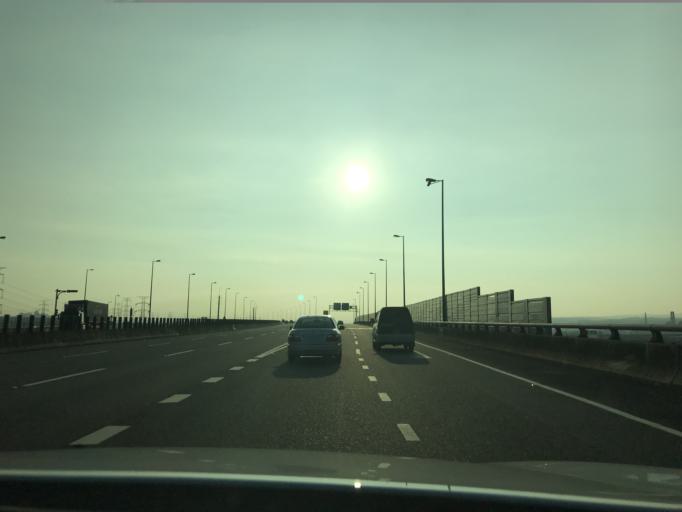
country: TW
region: Taiwan
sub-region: Changhua
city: Chang-hua
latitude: 24.1087
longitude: 120.5498
